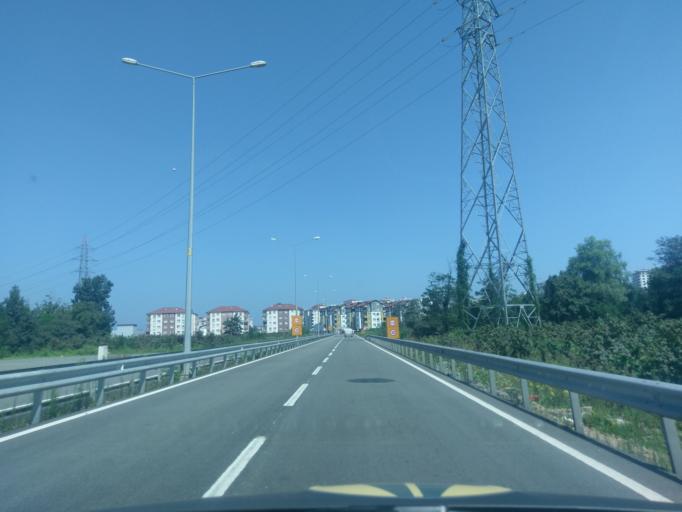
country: TR
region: Ordu
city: Ordu
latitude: 40.9599
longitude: 37.9060
